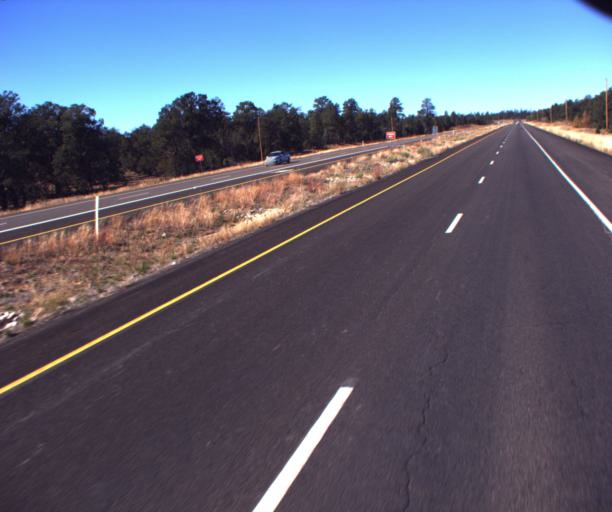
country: US
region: Arizona
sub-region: Apache County
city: Saint Michaels
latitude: 35.6600
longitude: -109.1576
